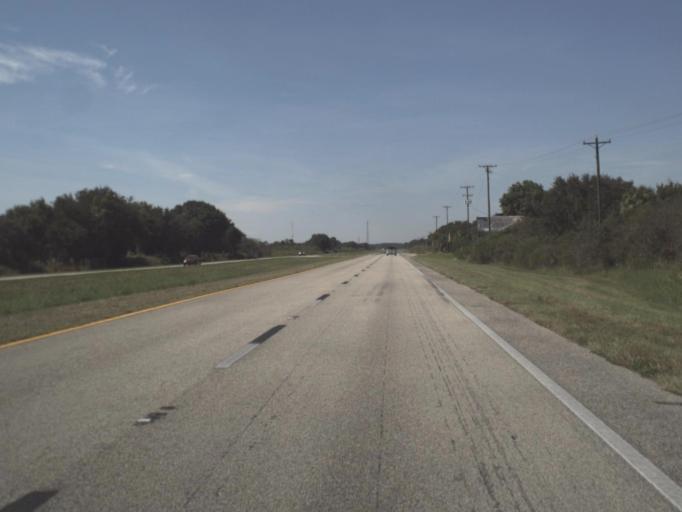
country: US
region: Florida
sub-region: Hendry County
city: Port LaBelle
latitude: 26.9161
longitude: -81.2883
